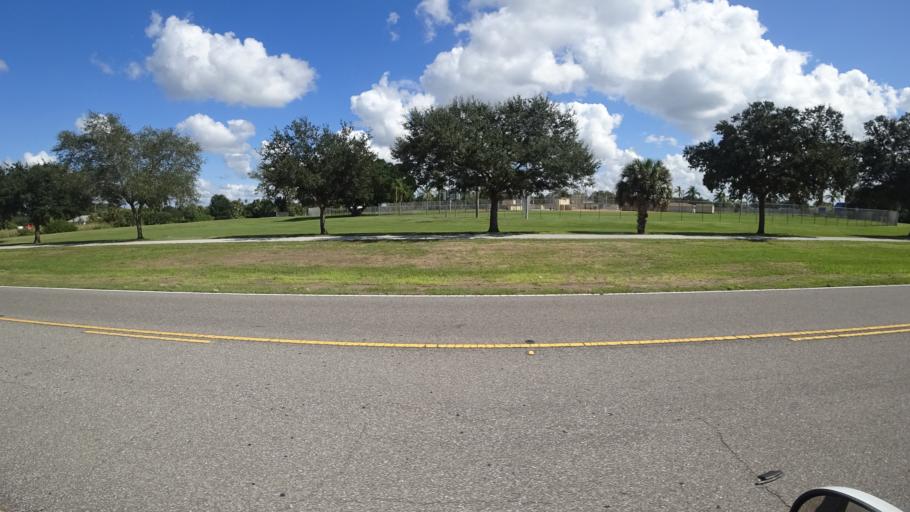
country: US
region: Florida
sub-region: Manatee County
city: West Bradenton
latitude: 27.4715
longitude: -82.6205
